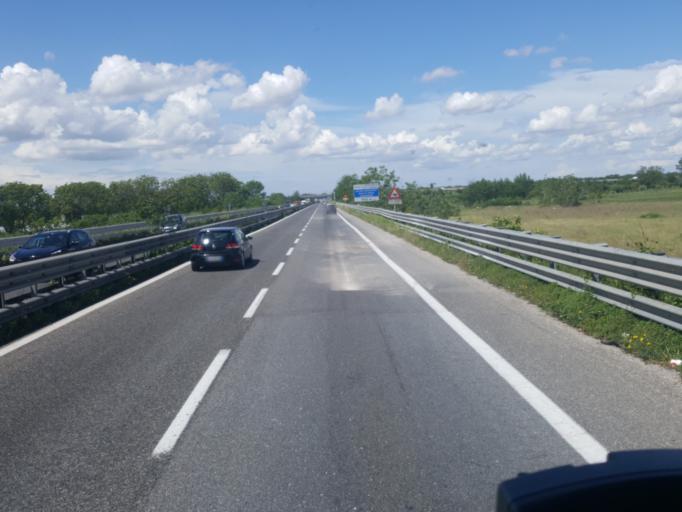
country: IT
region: Campania
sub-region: Provincia di Napoli
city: Pascarola
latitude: 40.9735
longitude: 14.3035
